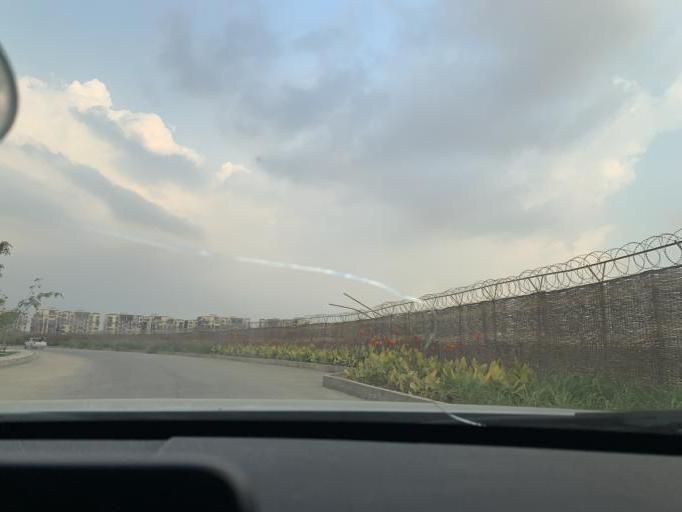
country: EG
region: Muhafazat al Qalyubiyah
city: Al Khankah
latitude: 30.0975
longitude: 31.6523
